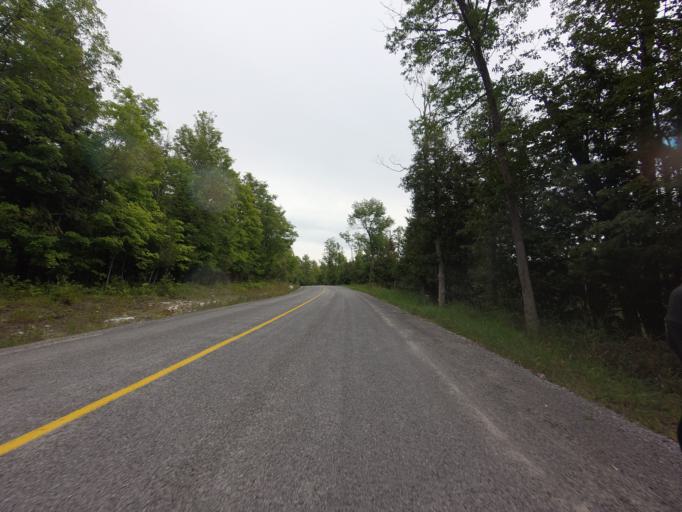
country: CA
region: Ontario
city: Perth
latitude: 44.8737
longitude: -76.5388
